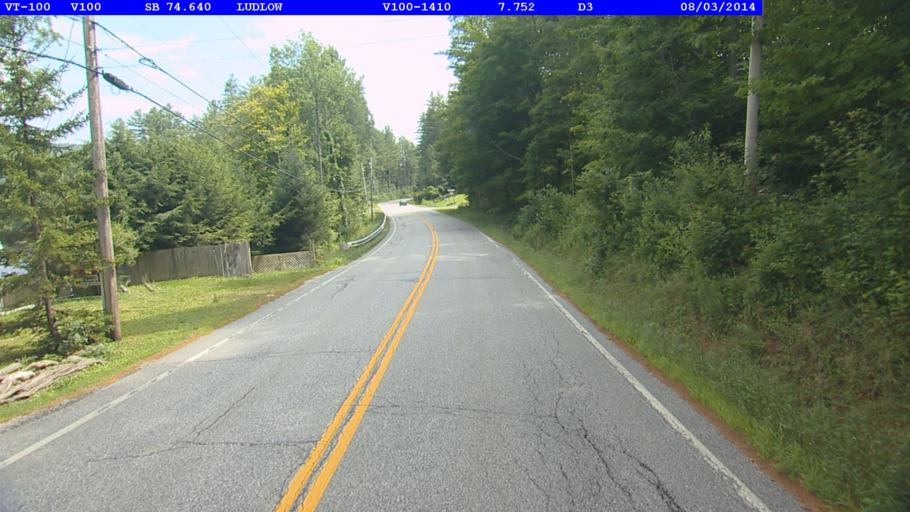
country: US
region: Vermont
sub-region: Windsor County
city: Chester
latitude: 43.4544
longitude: -72.7072
